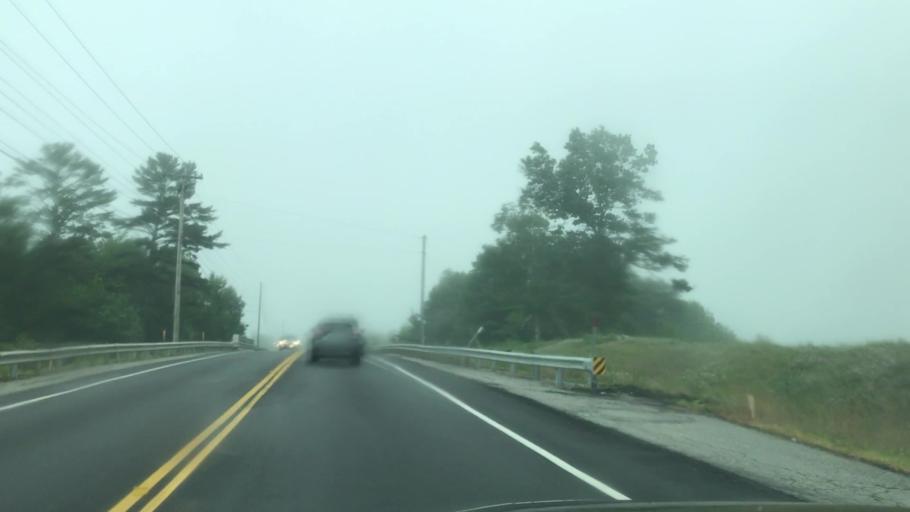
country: US
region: Maine
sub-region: Lincoln County
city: Waldoboro
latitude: 44.1044
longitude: -69.3656
